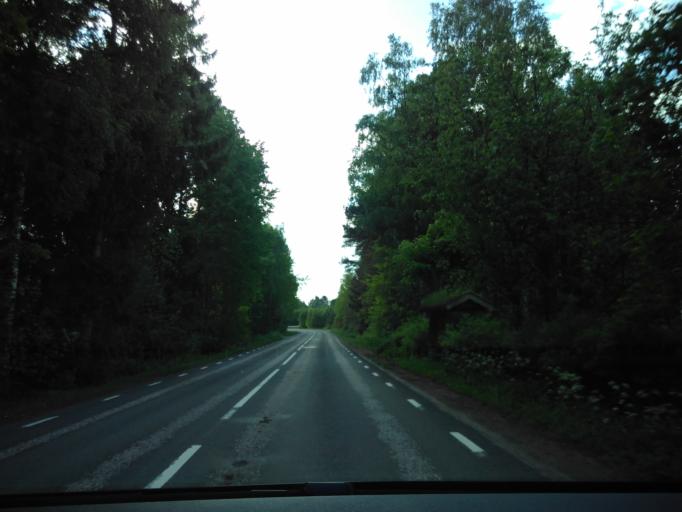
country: SE
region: Vaestra Goetaland
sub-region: Herrljunga Kommun
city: Herrljunga
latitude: 58.0635
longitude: 13.0827
